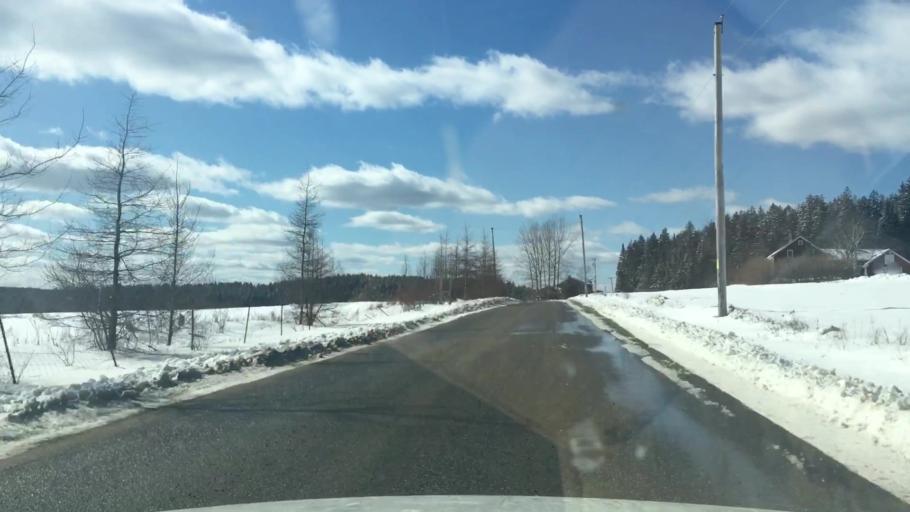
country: US
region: Maine
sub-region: Washington County
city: Machiasport
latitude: 44.6700
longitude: -67.4288
